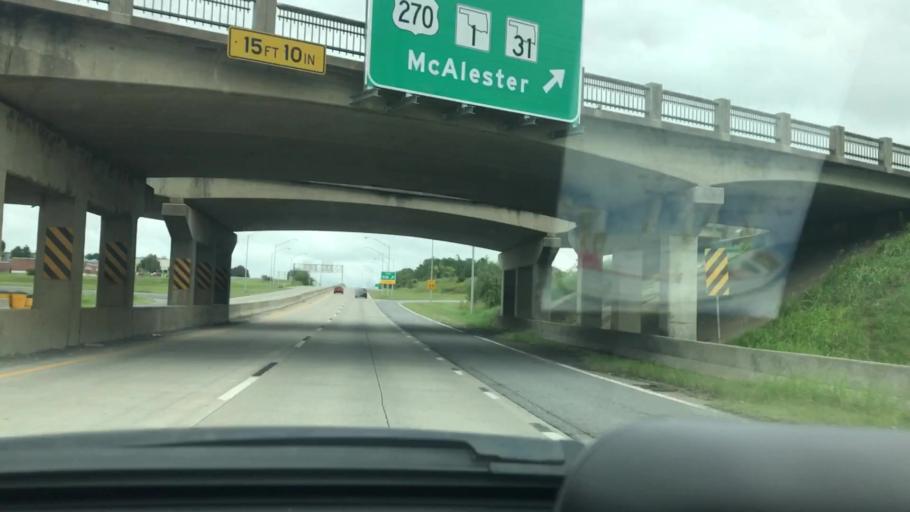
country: US
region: Oklahoma
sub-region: Pittsburg County
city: Krebs
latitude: 34.9273
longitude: -95.7404
